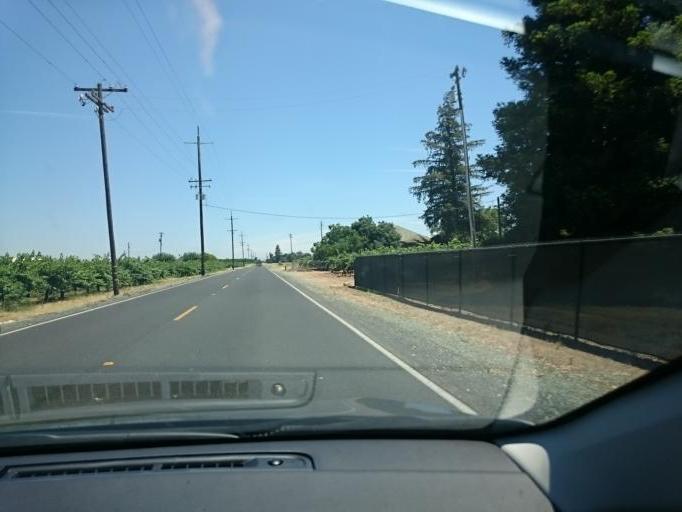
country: US
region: California
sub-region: San Joaquin County
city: Collierville
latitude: 38.1893
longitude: -121.2157
